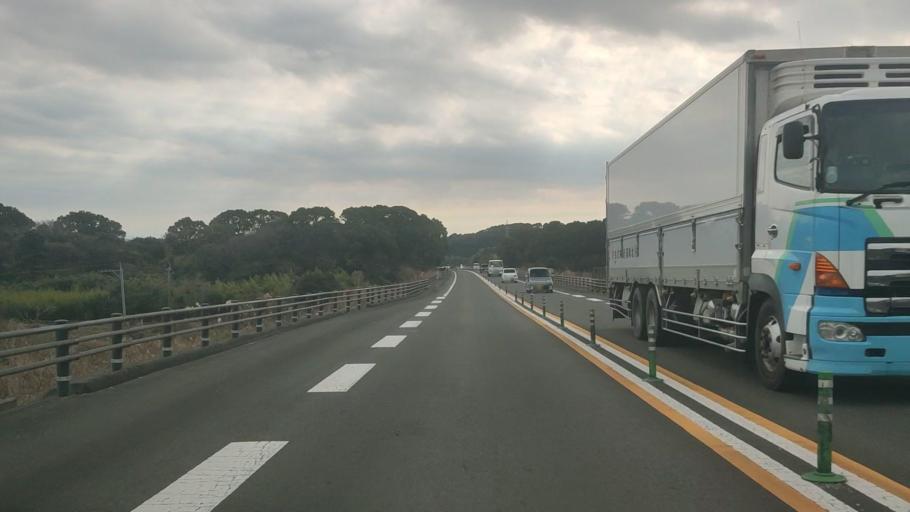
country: JP
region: Nagasaki
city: Shimabara
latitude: 32.7672
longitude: 130.3595
